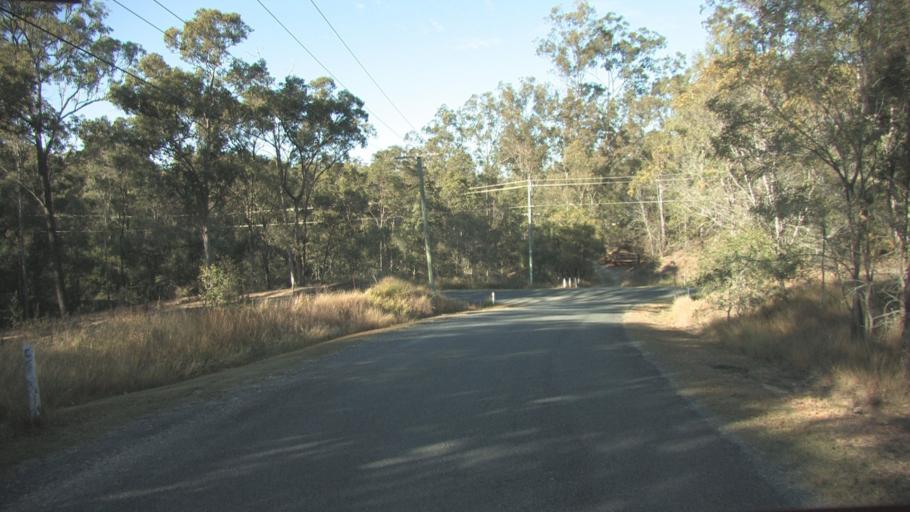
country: AU
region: Queensland
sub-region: Logan
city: Cedar Vale
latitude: -27.8370
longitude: 153.0889
